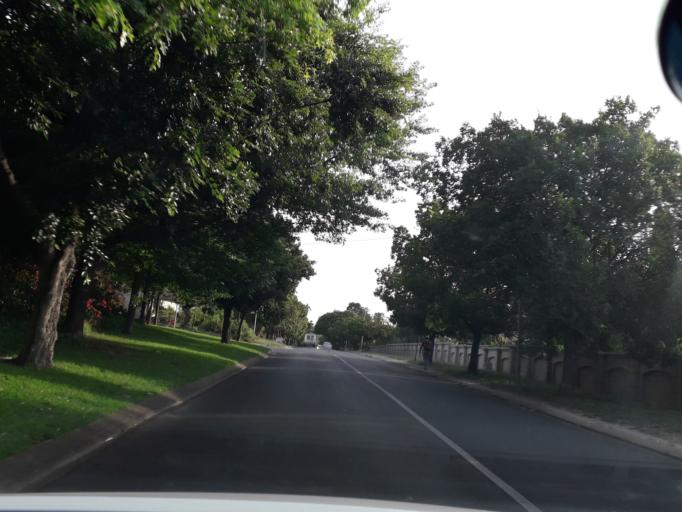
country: ZA
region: Gauteng
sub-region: City of Johannesburg Metropolitan Municipality
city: Diepsloot
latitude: -26.0682
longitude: 27.9870
